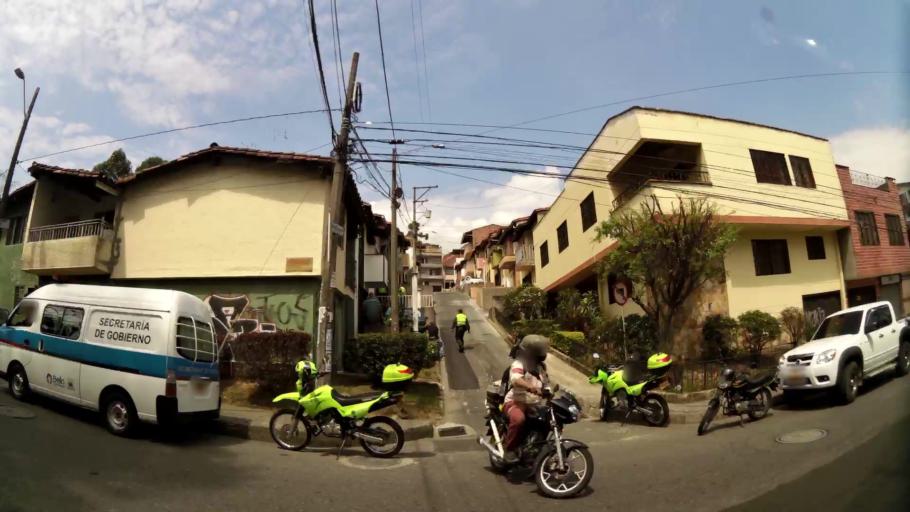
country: CO
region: Antioquia
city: Bello
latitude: 6.3124
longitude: -75.5635
